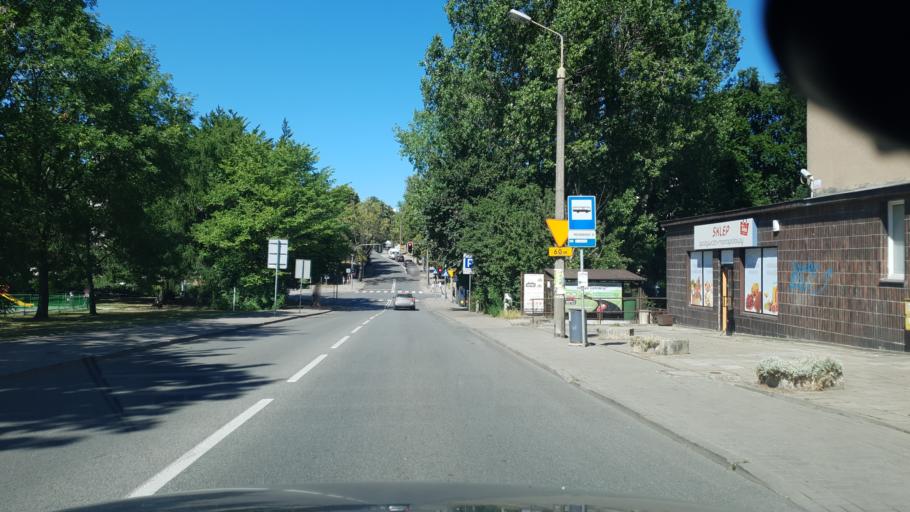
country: PL
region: Pomeranian Voivodeship
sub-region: Gdynia
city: Gdynia
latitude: 54.5075
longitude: 18.5447
